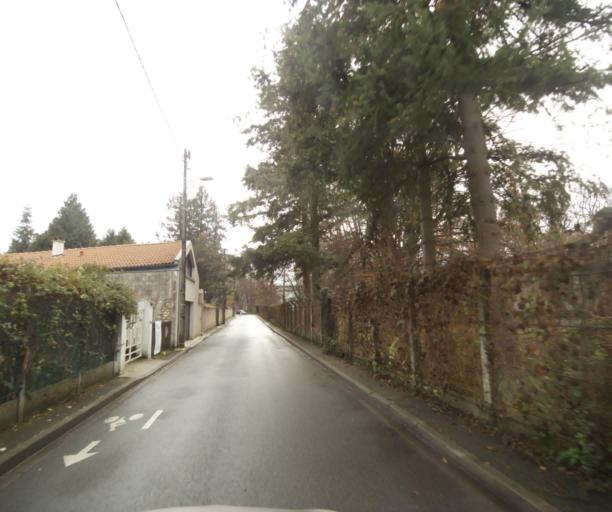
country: FR
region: Ile-de-France
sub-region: Departement de Seine-et-Marne
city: Avon
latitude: 48.4002
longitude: 2.7208
